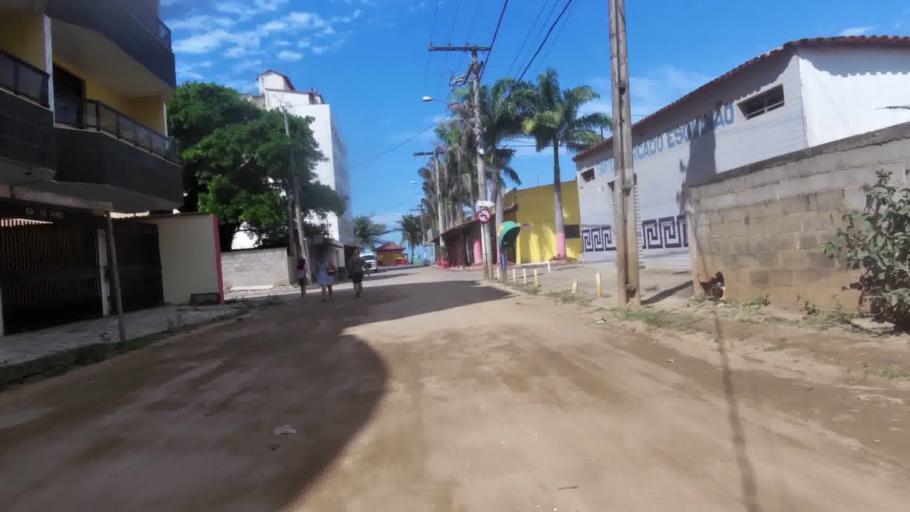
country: BR
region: Espirito Santo
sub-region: Piuma
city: Piuma
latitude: -20.8434
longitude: -40.7360
